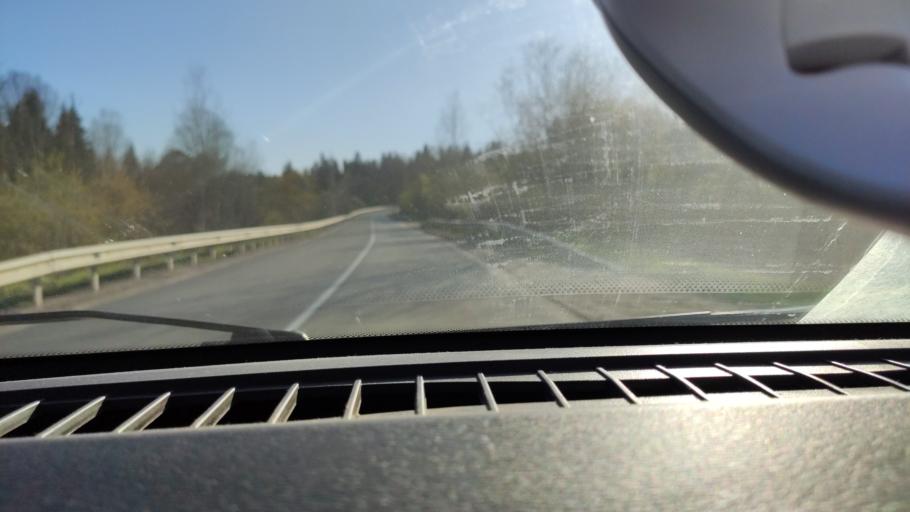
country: RU
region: Perm
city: Novyye Lyady
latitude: 58.1218
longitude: 56.4562
